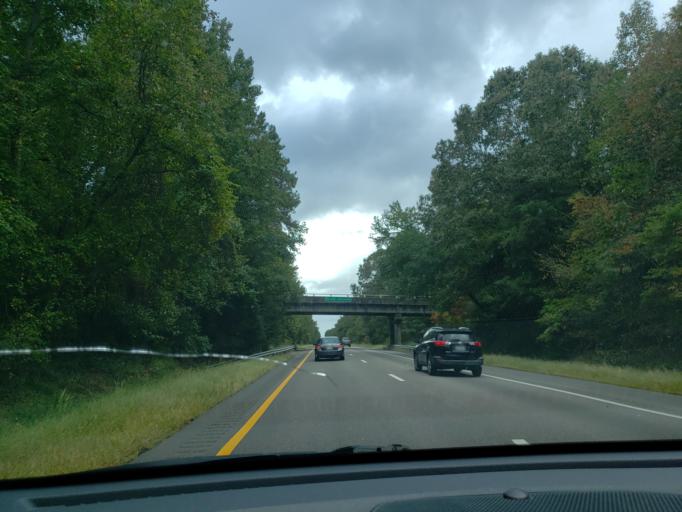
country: US
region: Virginia
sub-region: Mecklenburg County
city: Bracey
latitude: 36.6608
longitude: -78.1338
